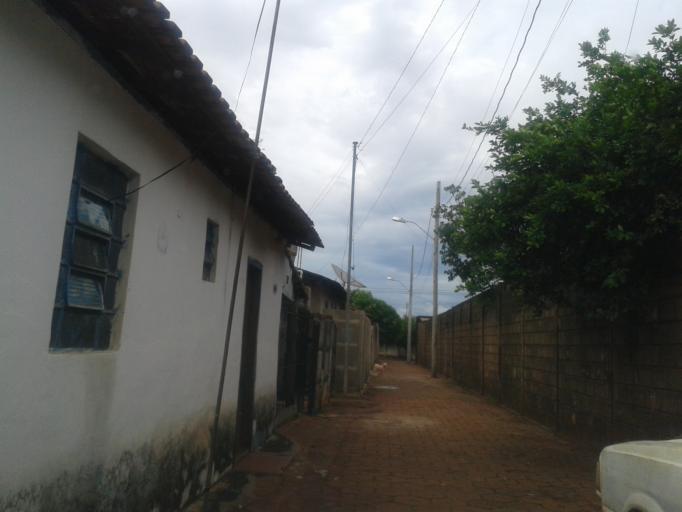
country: BR
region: Minas Gerais
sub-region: Centralina
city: Centralina
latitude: -18.7208
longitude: -49.1957
